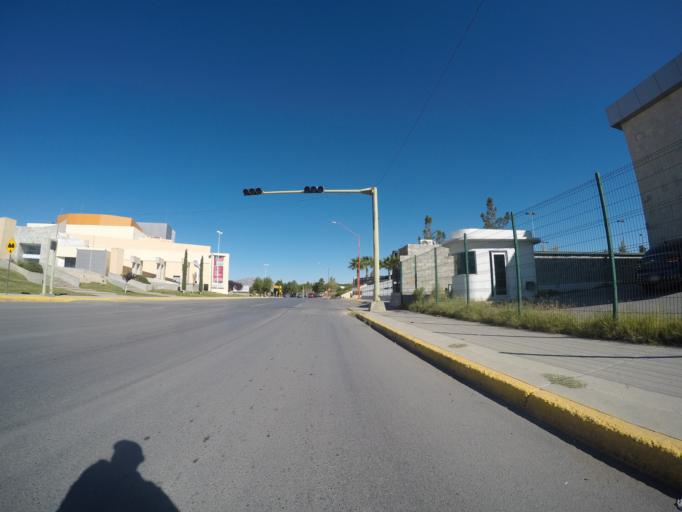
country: MX
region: Chihuahua
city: Ciudad Juarez
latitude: 31.7429
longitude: -106.4439
